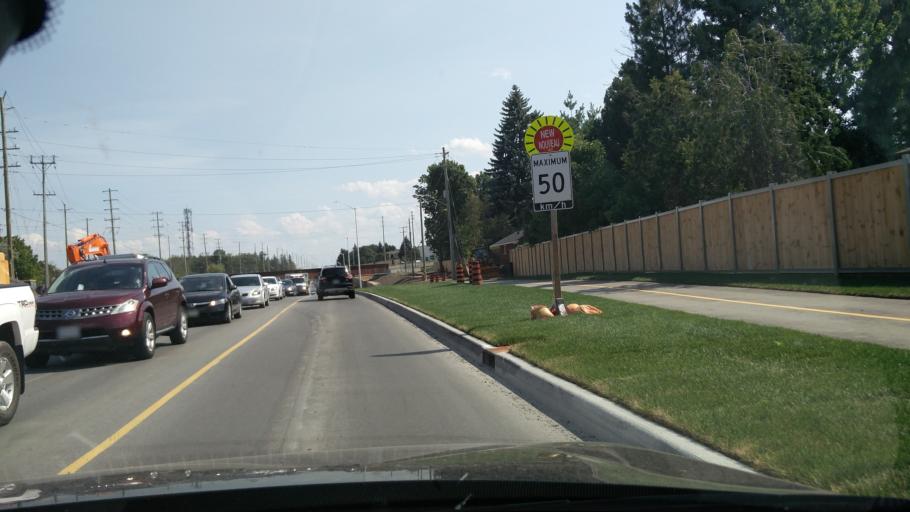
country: CA
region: Ontario
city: Bells Corners
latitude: 45.2815
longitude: -75.7532
